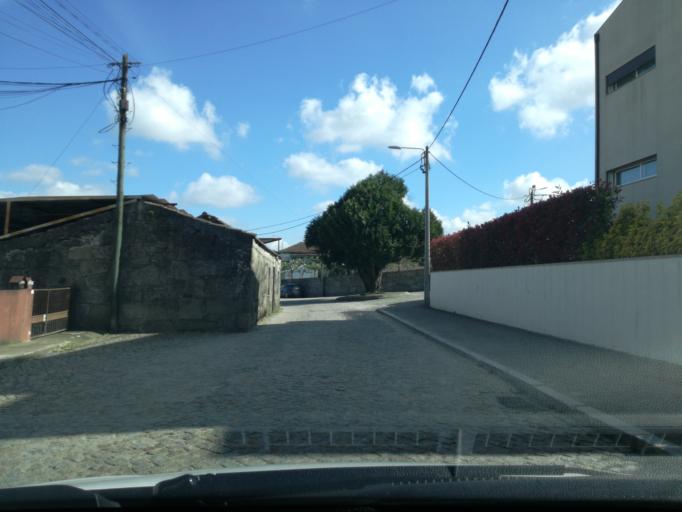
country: PT
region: Porto
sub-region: Valongo
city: Ermesinde
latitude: 41.2307
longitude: -8.5609
